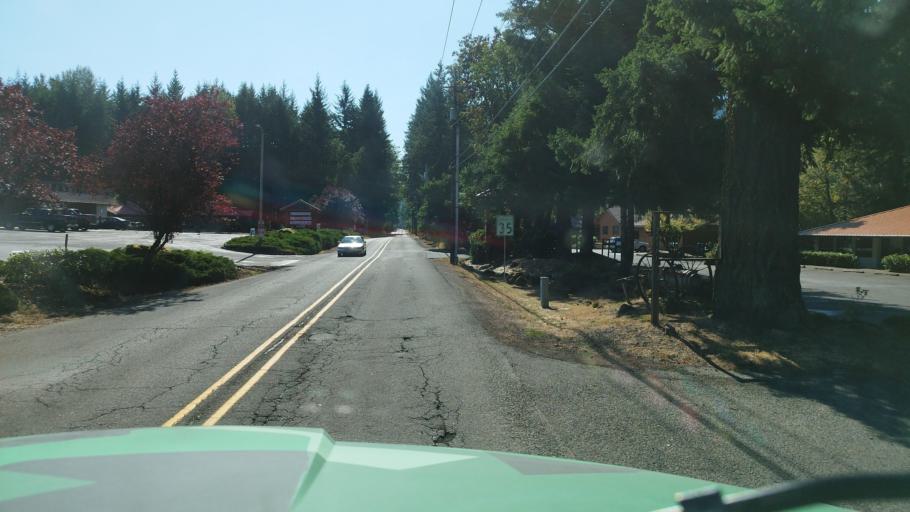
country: US
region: Oregon
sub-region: Clackamas County
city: Mount Hood Village
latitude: 45.3473
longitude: -121.9635
